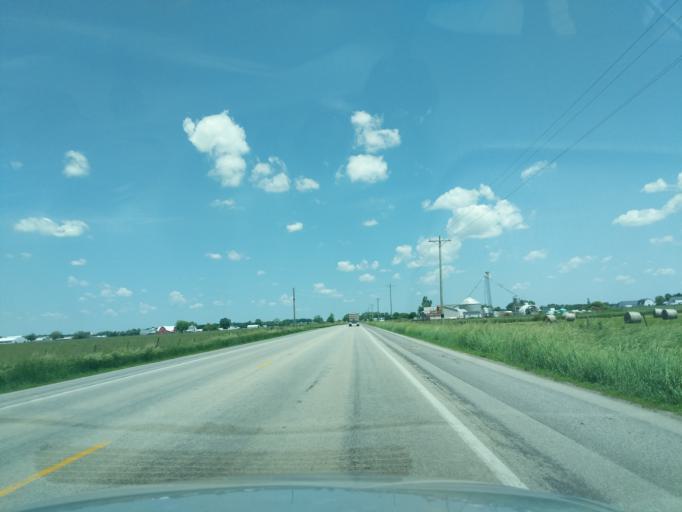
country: US
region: Indiana
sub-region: LaGrange County
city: Topeka
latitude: 41.6032
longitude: -85.5790
